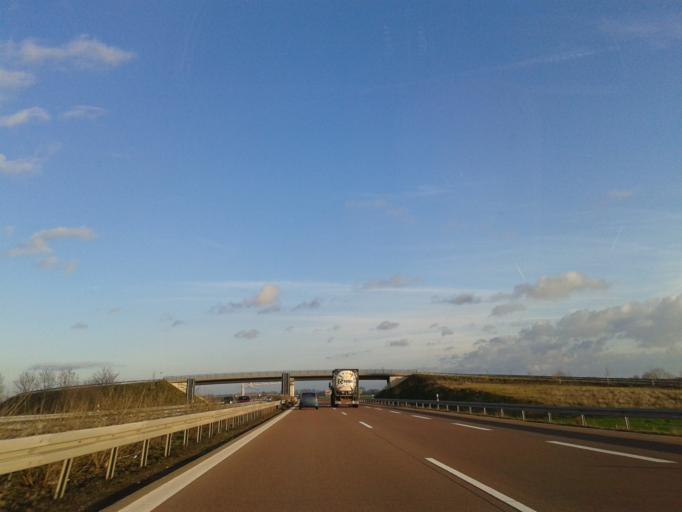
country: DE
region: Saxony-Anhalt
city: Schafstadt
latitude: 51.3997
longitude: 11.7313
